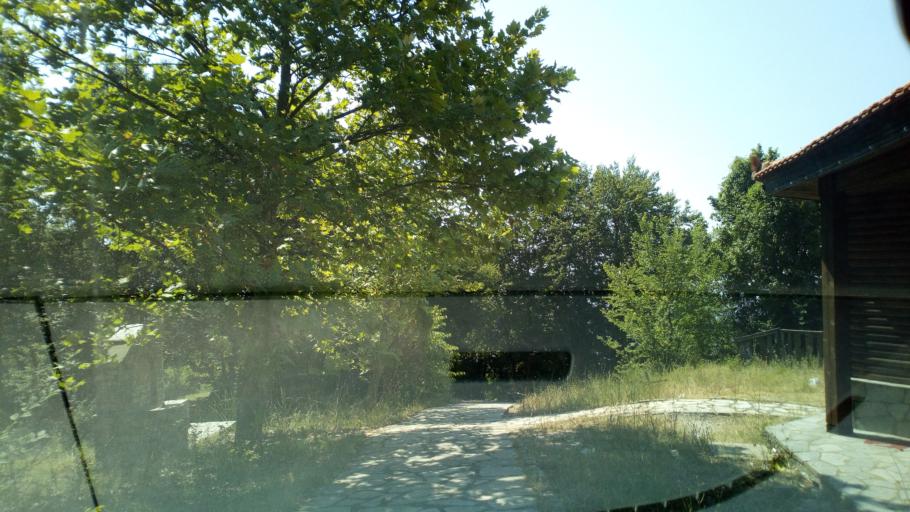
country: GR
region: Central Macedonia
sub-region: Nomos Thessalonikis
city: Sochos
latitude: 40.8263
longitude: 23.3568
